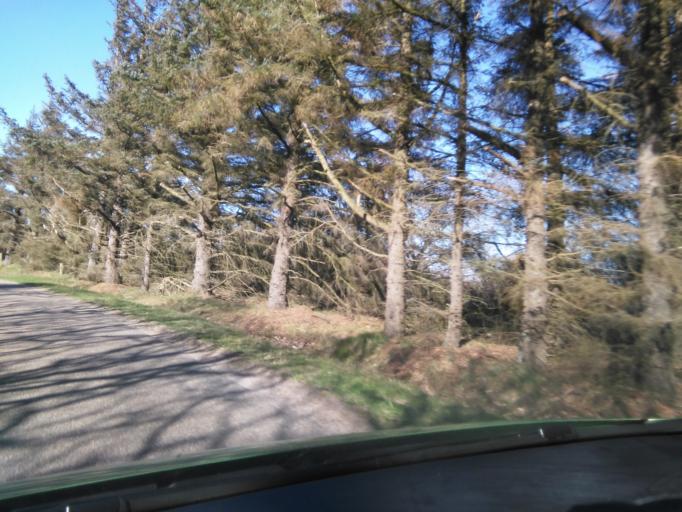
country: DK
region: South Denmark
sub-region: Varde Kommune
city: Oksbol
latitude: 55.6860
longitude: 8.1895
